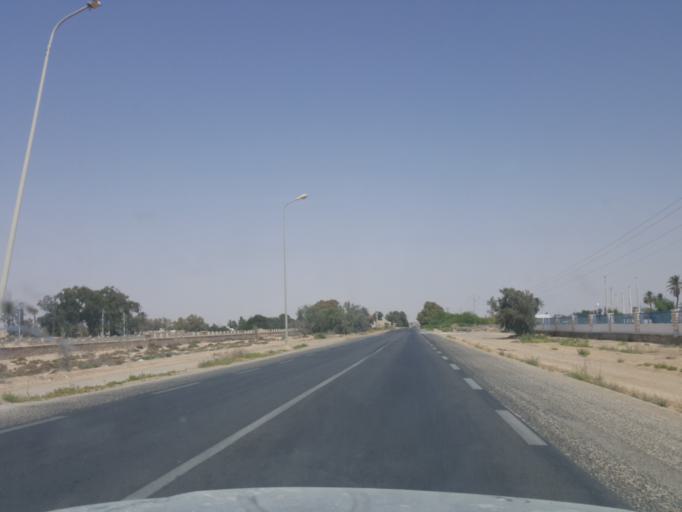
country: TN
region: Qabis
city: Gabes
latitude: 33.9819
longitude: 10.0058
